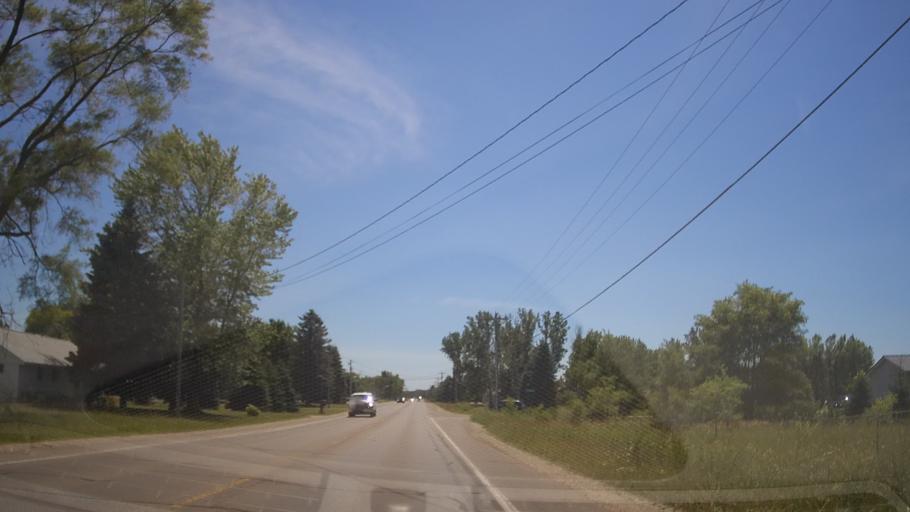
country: US
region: Michigan
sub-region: Grand Traverse County
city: Traverse City
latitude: 44.6755
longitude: -85.6899
